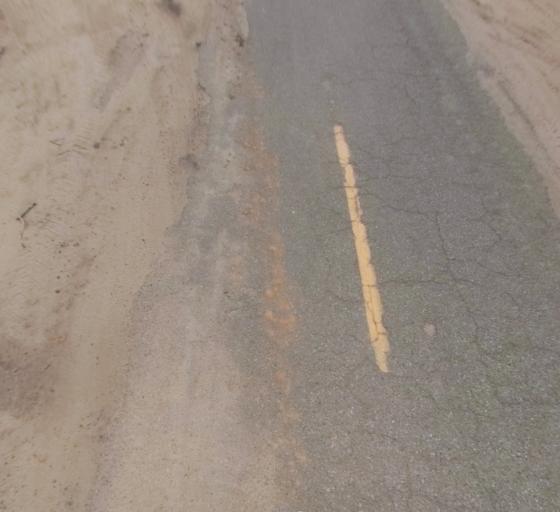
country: US
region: California
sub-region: Madera County
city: Fairmead
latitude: 37.0546
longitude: -120.1607
